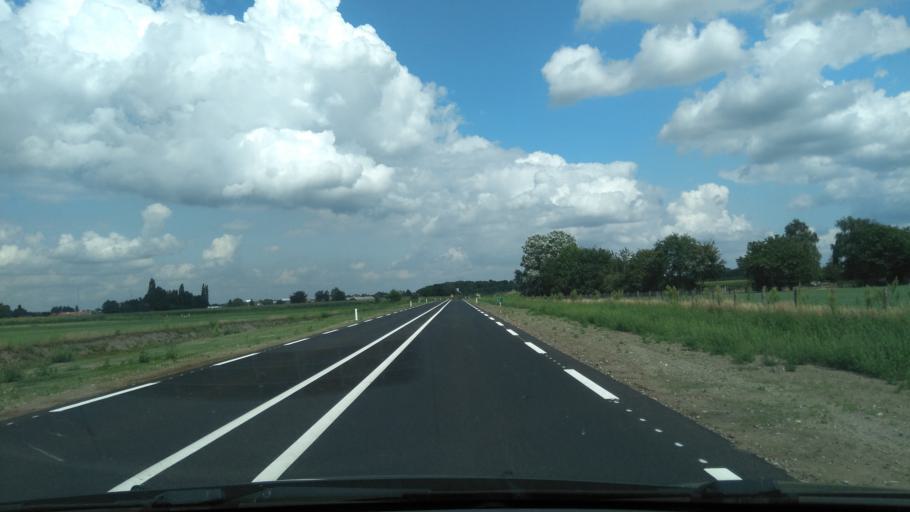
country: NL
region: North Brabant
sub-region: Gemeente Baarle-Nassau
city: Baarle-Nassau
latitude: 51.4323
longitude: 4.9396
